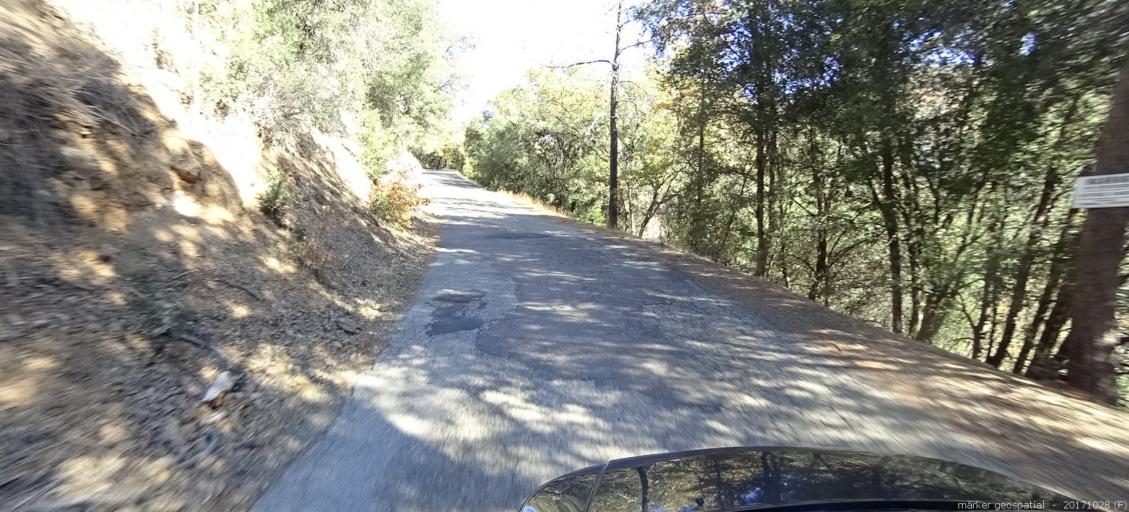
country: US
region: California
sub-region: Trinity County
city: Lewiston
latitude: 40.7954
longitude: -122.6103
